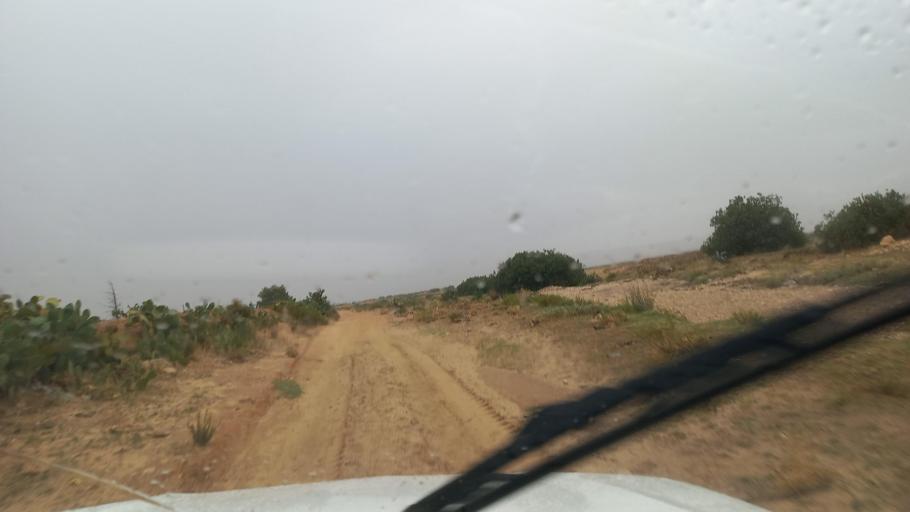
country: TN
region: Al Qasrayn
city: Kasserine
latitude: 35.2700
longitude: 8.9459
